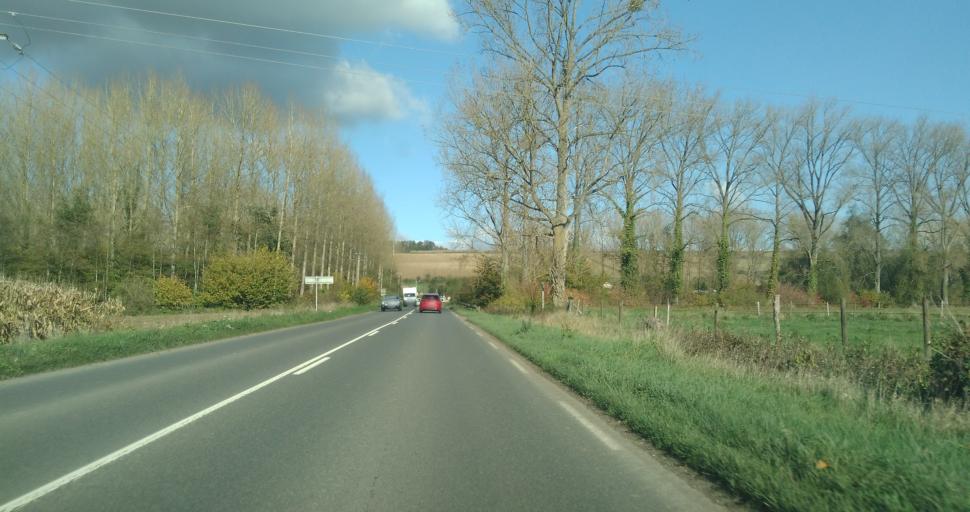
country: FR
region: Picardie
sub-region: Departement de la Somme
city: Doullens
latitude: 50.1647
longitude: 2.3007
